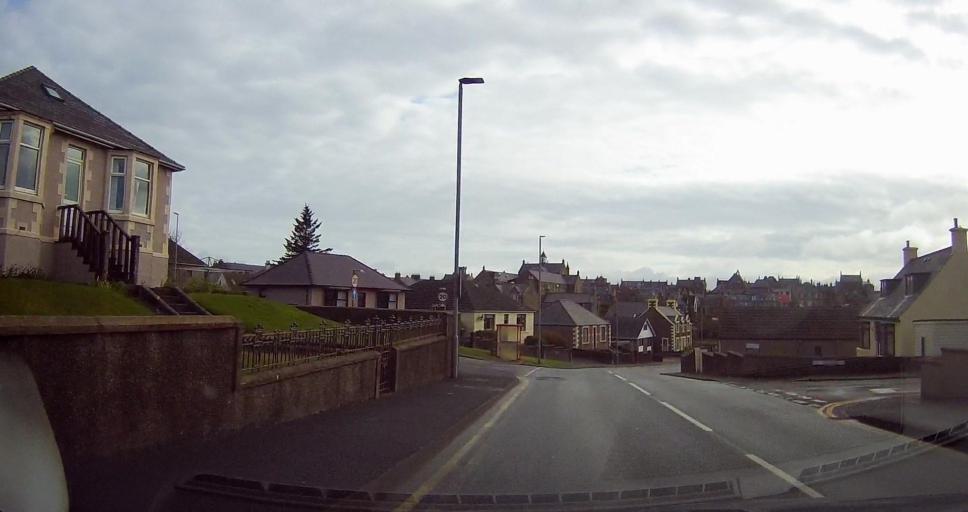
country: GB
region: Scotland
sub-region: Shetland Islands
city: Lerwick
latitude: 60.1513
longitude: -1.1529
